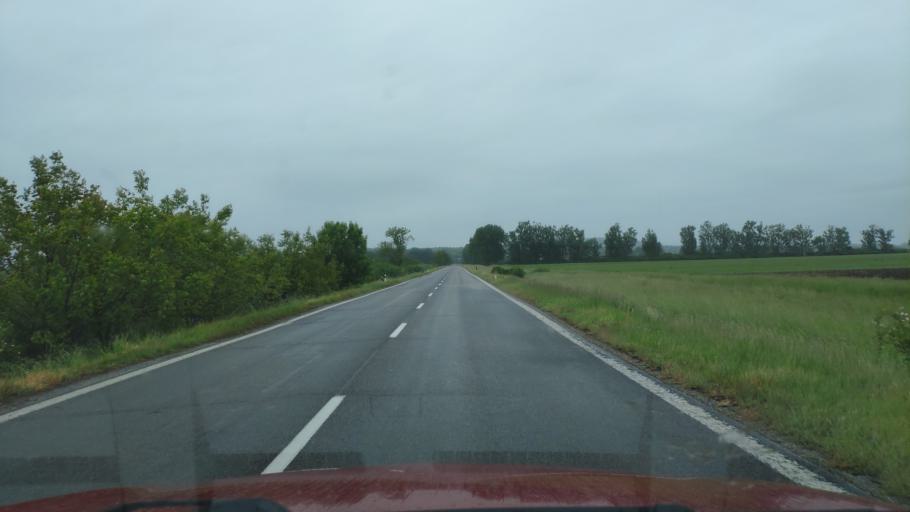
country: HU
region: Borsod-Abauj-Zemplen
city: Ricse
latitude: 48.4332
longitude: 21.8945
